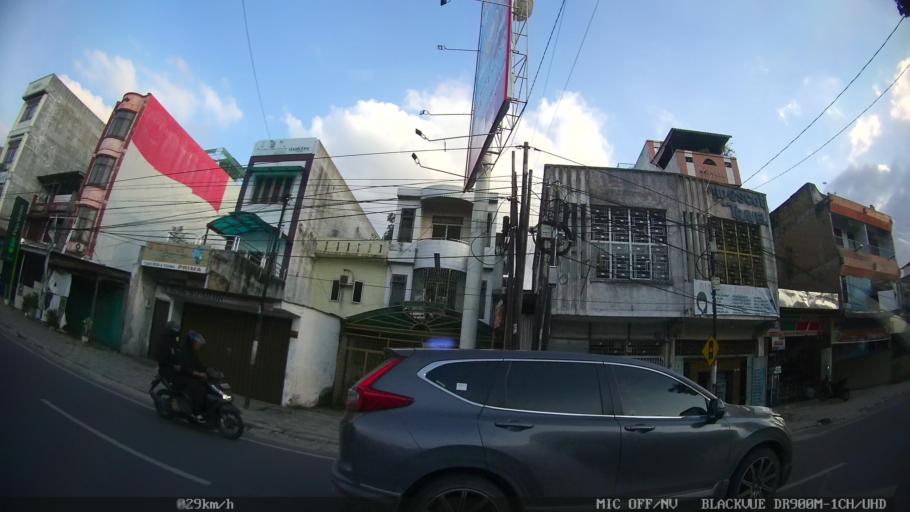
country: ID
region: North Sumatra
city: Medan
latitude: 3.5902
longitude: 98.6593
